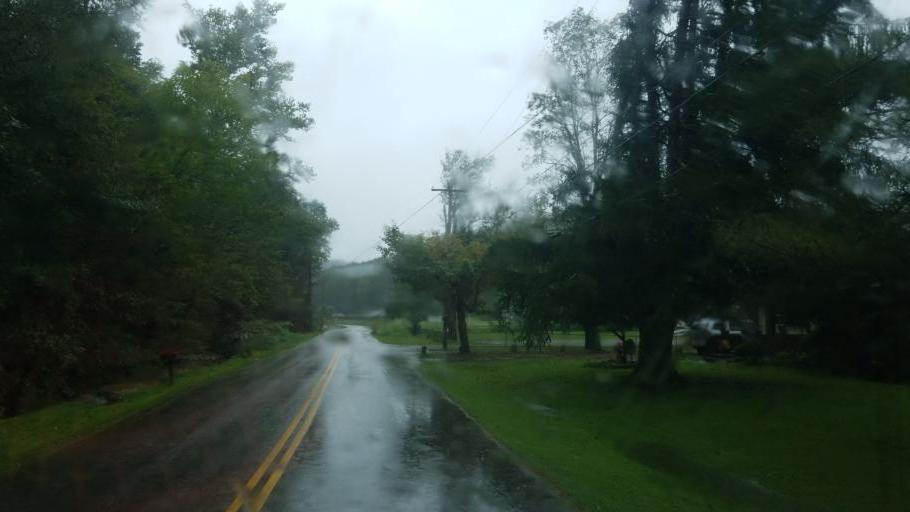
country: US
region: Ohio
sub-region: Scioto County
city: West Portsmouth
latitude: 38.7416
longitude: -83.0747
